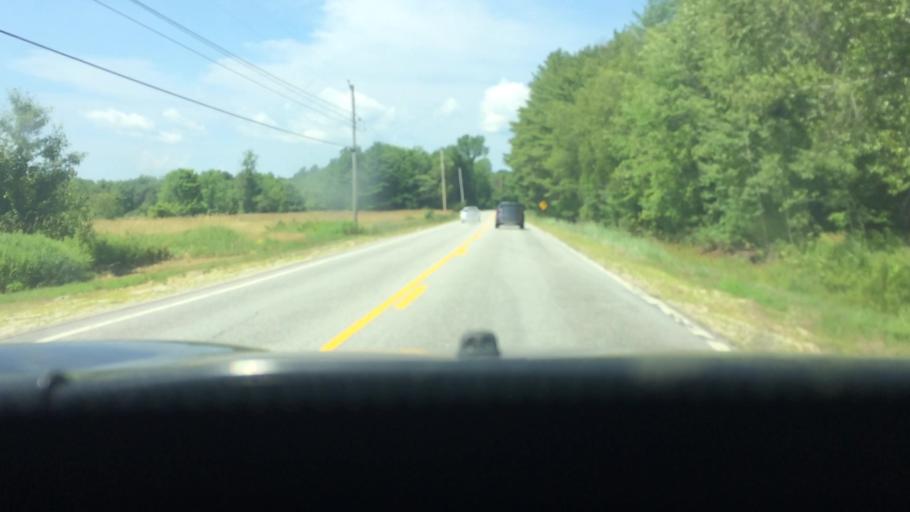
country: US
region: Maine
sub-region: Oxford County
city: Oxford
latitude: 44.1323
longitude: -70.4446
